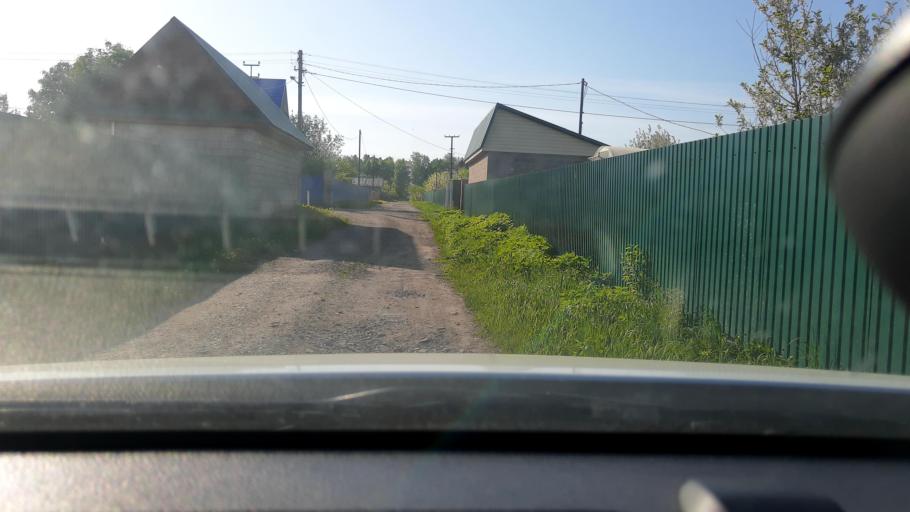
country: RU
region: Bashkortostan
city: Kabakovo
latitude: 54.4712
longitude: 55.9278
